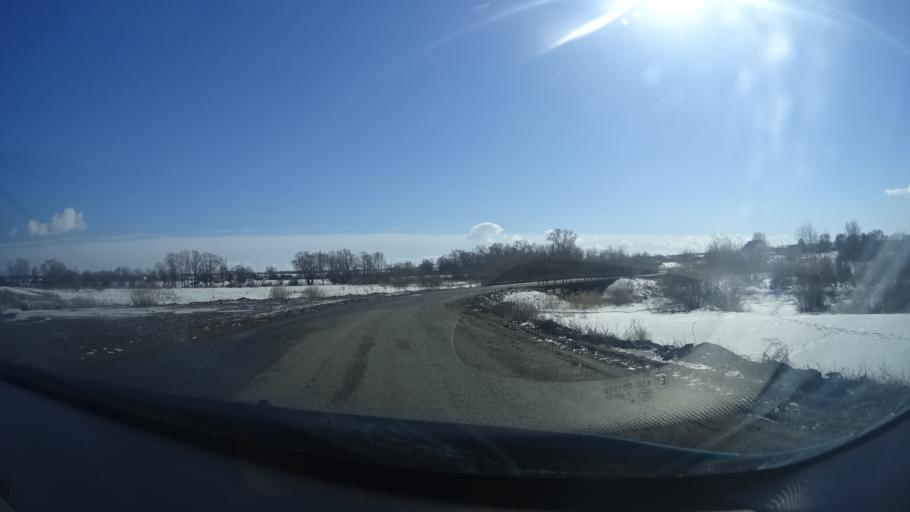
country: RU
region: Bashkortostan
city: Avdon
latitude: 54.5854
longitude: 55.8581
